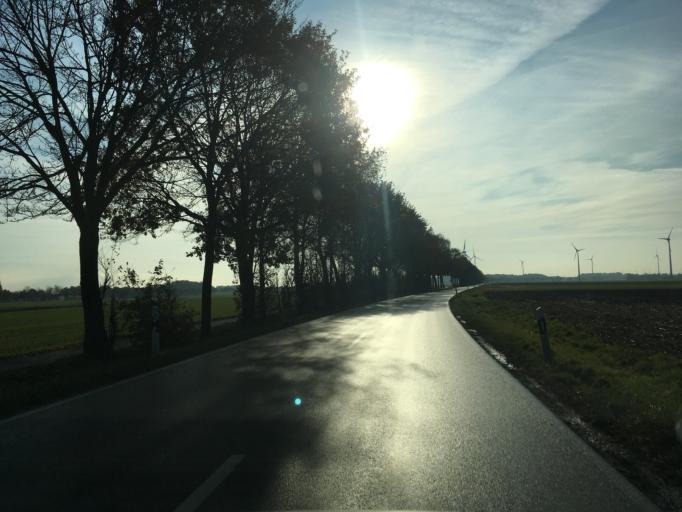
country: DE
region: North Rhine-Westphalia
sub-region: Regierungsbezirk Munster
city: Ahaus
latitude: 52.0656
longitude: 6.9866
